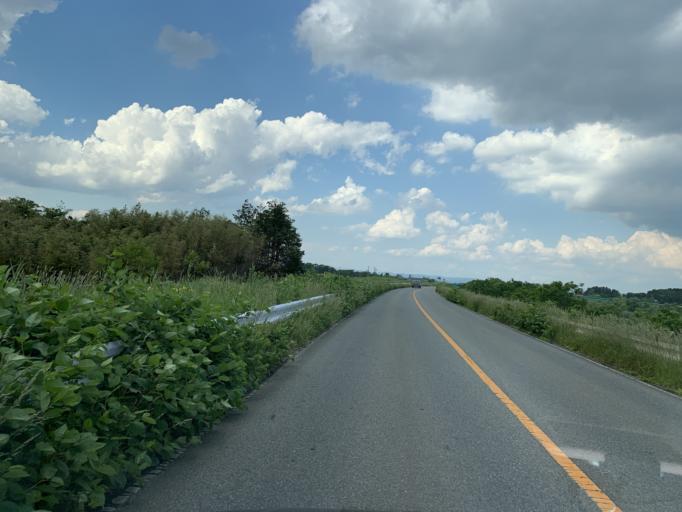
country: JP
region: Miyagi
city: Wakuya
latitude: 38.6393
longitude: 141.2054
